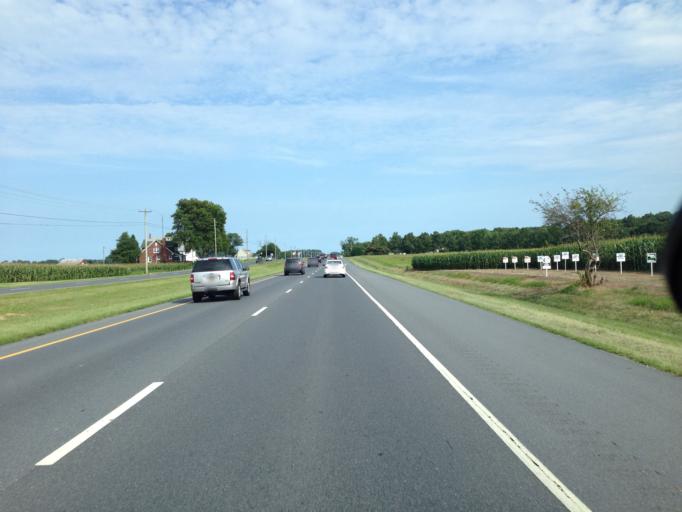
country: US
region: Delaware
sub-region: Sussex County
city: Milton
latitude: 38.7747
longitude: -75.2256
